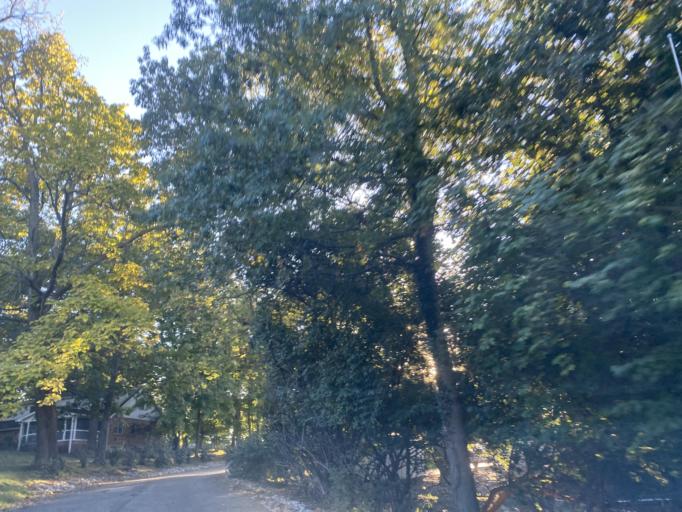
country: US
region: Kentucky
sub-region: Campbell County
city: Dayton
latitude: 39.1048
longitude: -84.4506
